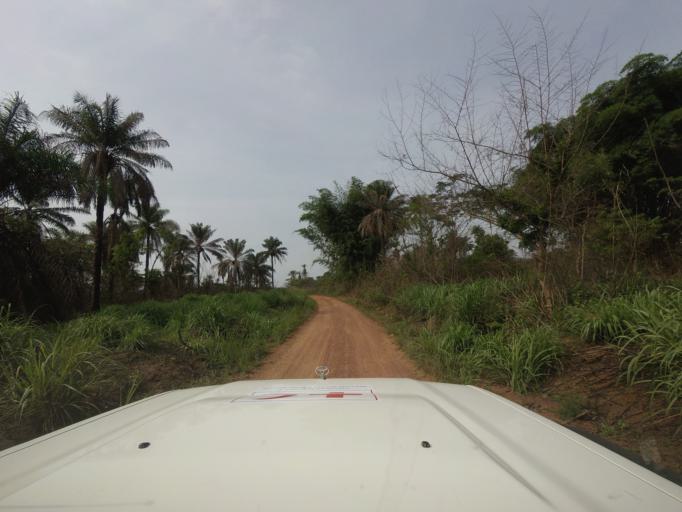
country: GN
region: Nzerekore
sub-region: Macenta
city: Macenta
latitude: 8.5060
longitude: -9.5304
